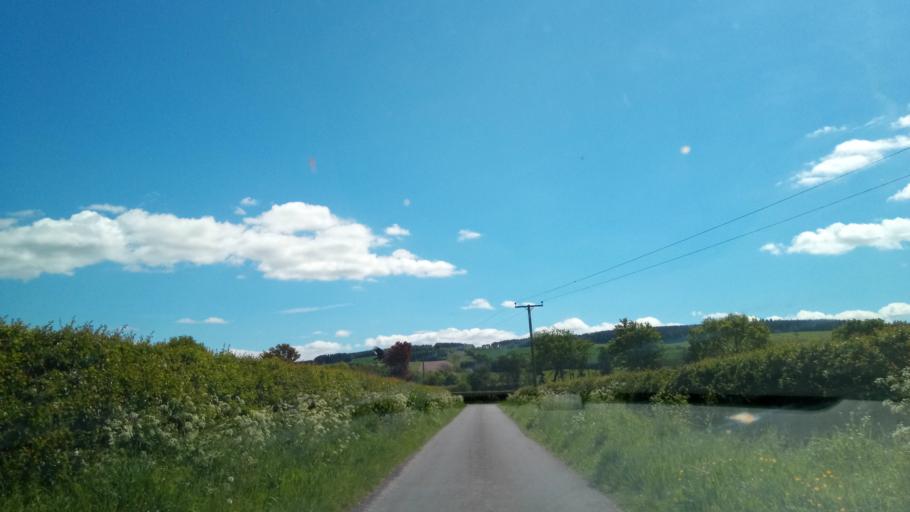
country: GB
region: Scotland
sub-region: The Scottish Borders
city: Saint Boswells
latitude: 55.4686
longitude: -2.6753
